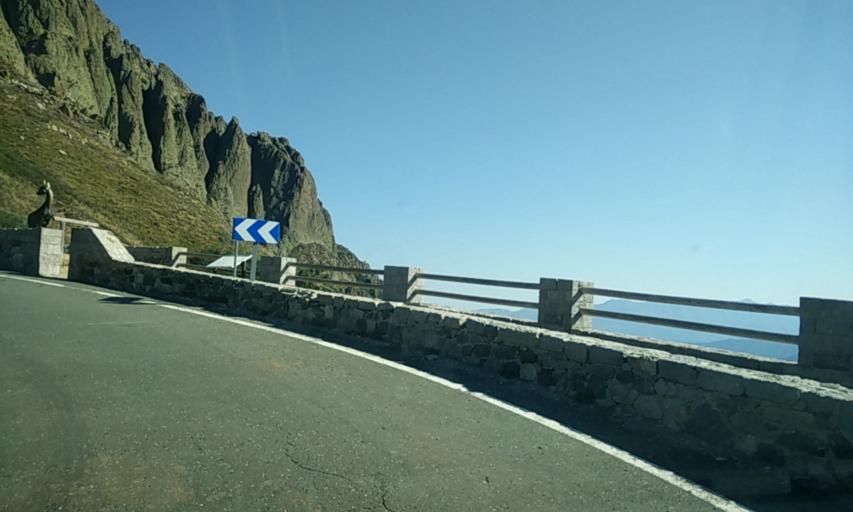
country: ES
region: Cantabria
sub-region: Provincia de Cantabria
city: Camaleno
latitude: 43.0766
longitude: -4.7331
